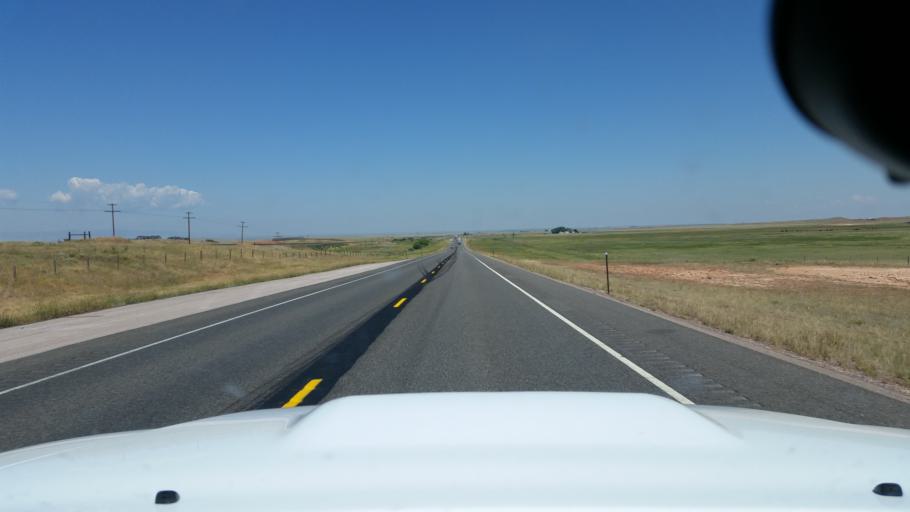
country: US
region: Wyoming
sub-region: Albany County
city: Laramie
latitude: 41.1541
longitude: -105.5721
